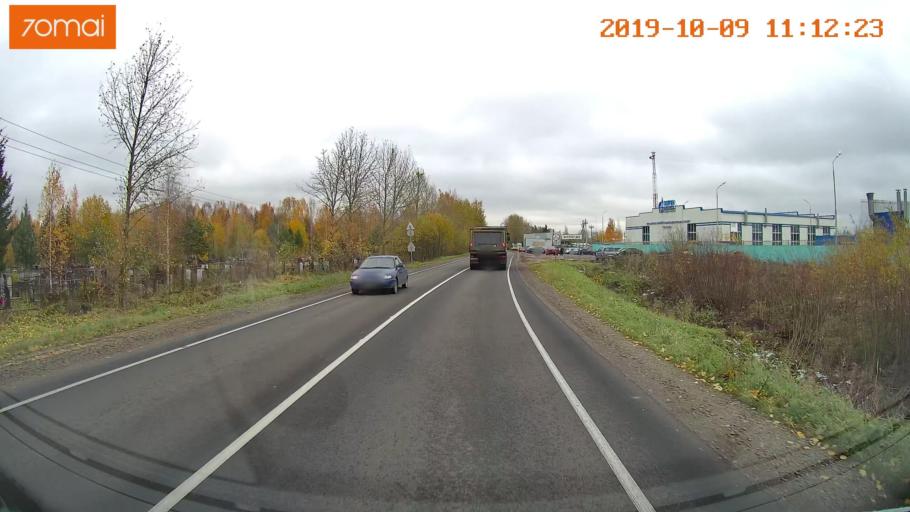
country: RU
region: Vologda
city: Vologda
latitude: 59.1771
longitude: 39.8299
